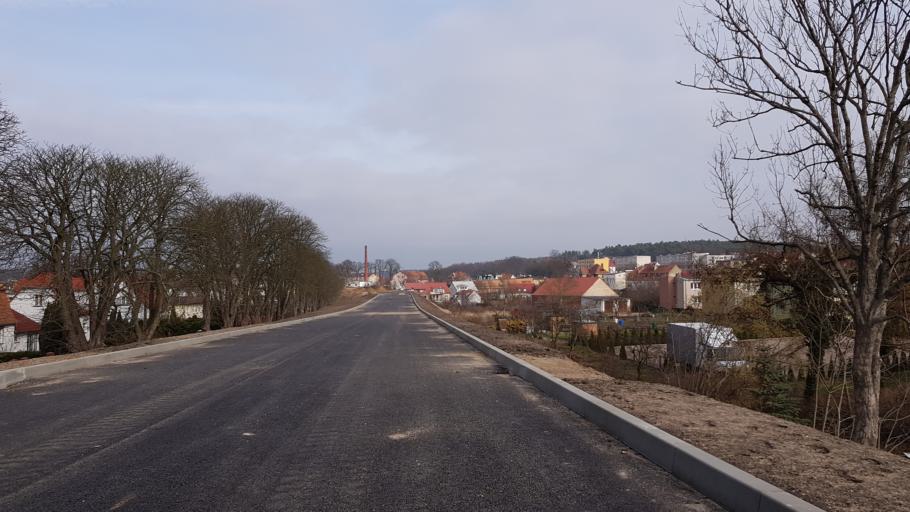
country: PL
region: West Pomeranian Voivodeship
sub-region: Powiat mysliborski
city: Barlinek
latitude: 52.9955
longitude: 15.2151
